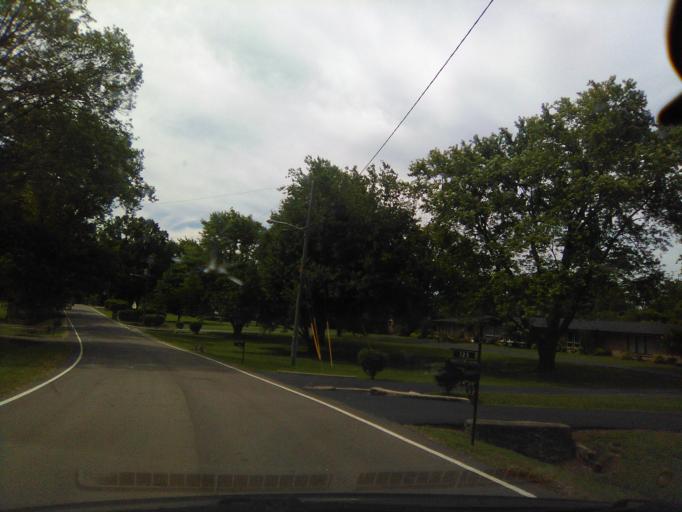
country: US
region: Tennessee
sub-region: Davidson County
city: Belle Meade
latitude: 36.0993
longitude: -86.8797
